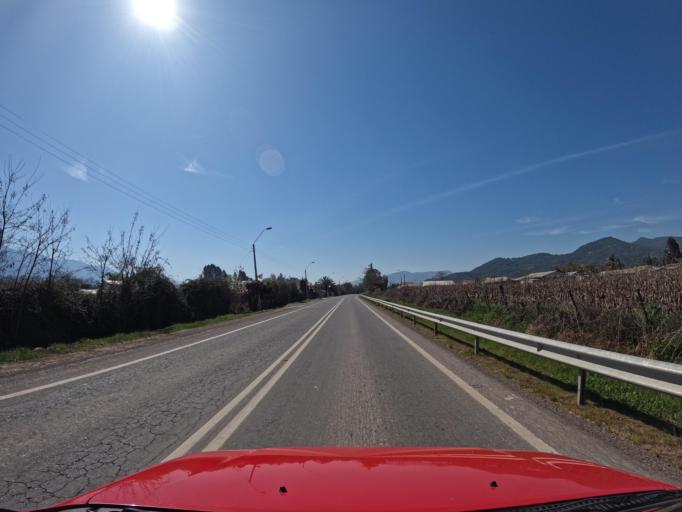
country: CL
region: Maule
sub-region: Provincia de Curico
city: Rauco
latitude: -35.0528
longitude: -71.4787
